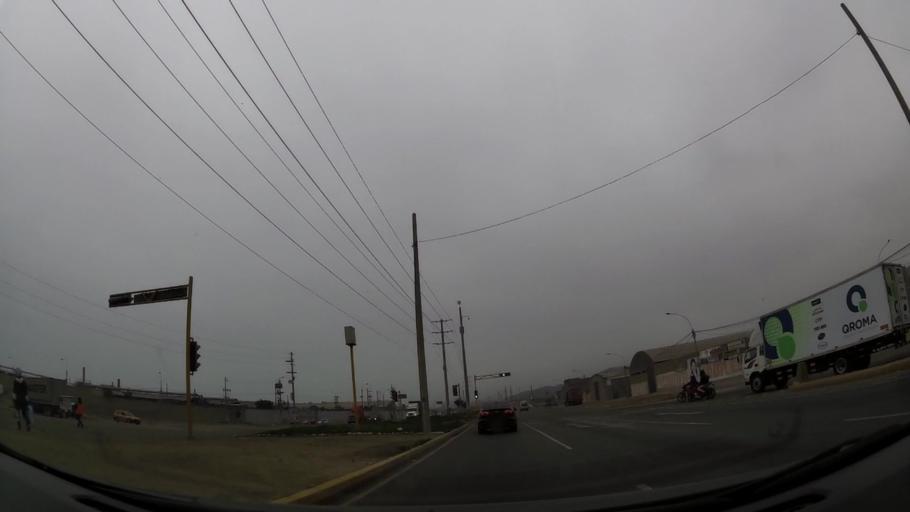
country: PE
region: Lima
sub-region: Lima
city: Independencia
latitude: -11.9698
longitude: -77.1254
